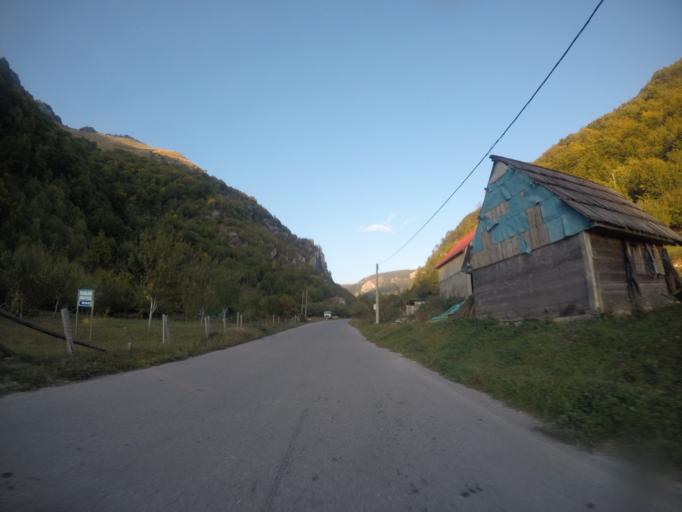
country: ME
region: Opstina Kolasin
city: Kolasin
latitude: 42.8336
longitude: 19.5605
